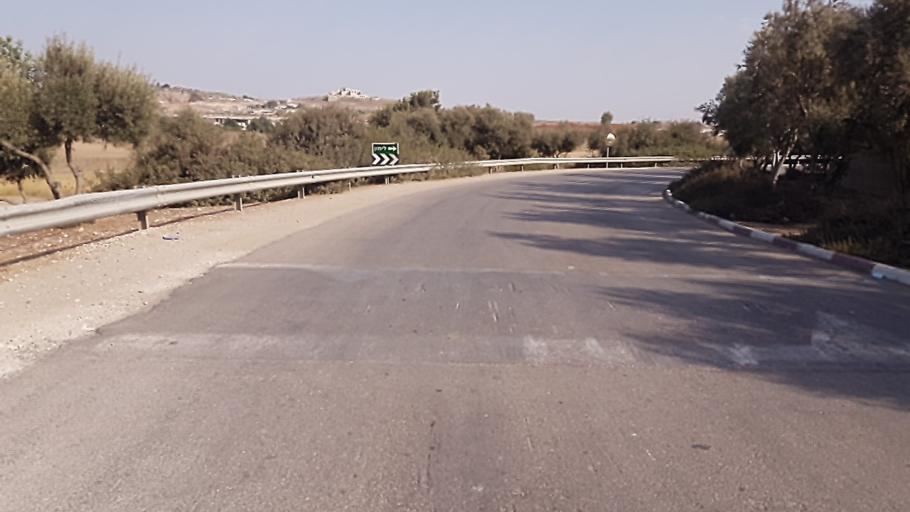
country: IL
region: Central District
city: Rosh Ha'Ayin
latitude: 32.0840
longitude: 34.9440
